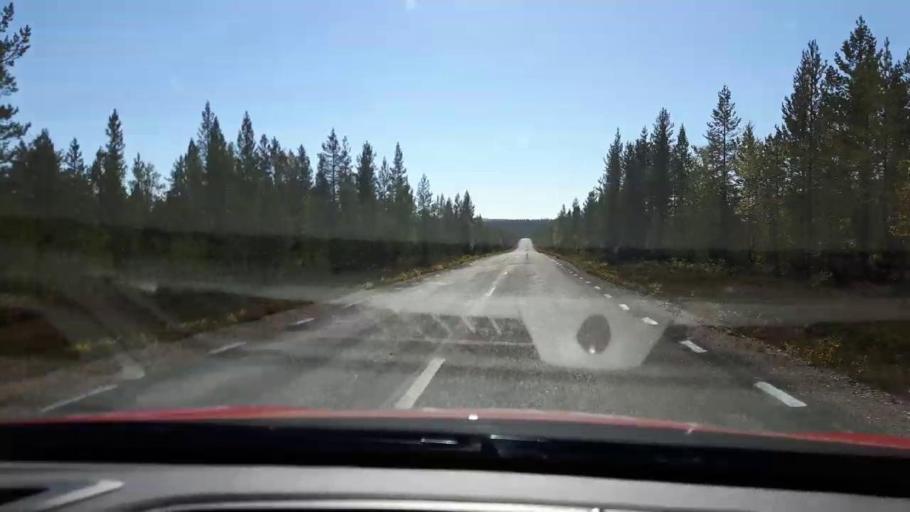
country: SE
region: Jaemtland
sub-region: Harjedalens Kommun
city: Sveg
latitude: 61.7191
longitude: 14.1681
